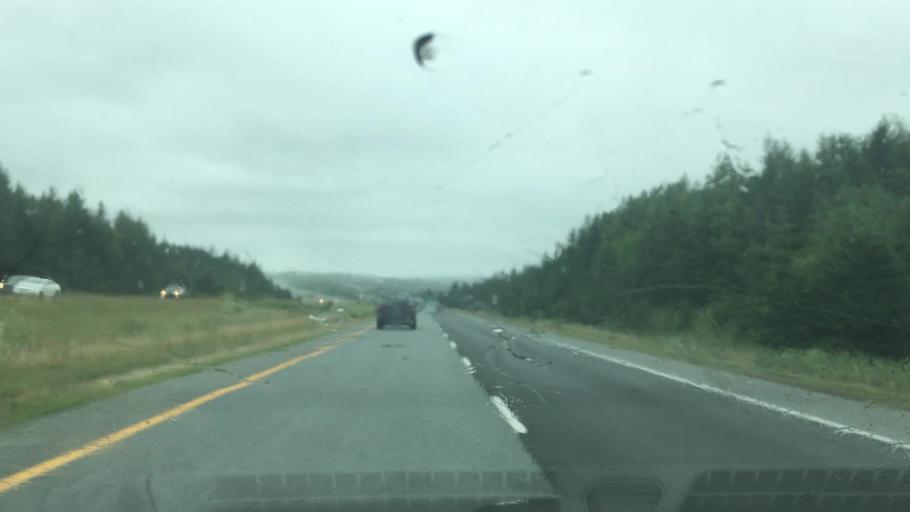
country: CA
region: Nova Scotia
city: Truro
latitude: 45.2422
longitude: -63.2928
